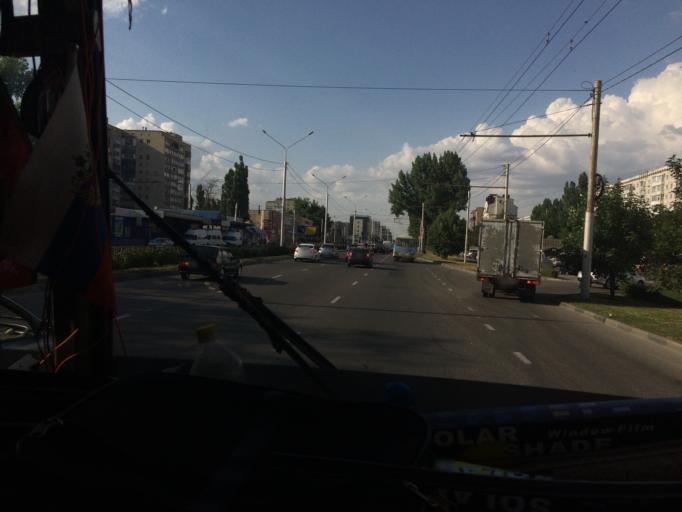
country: RU
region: Stavropol'skiy
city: Stavropol'
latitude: 45.0137
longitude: 41.9307
